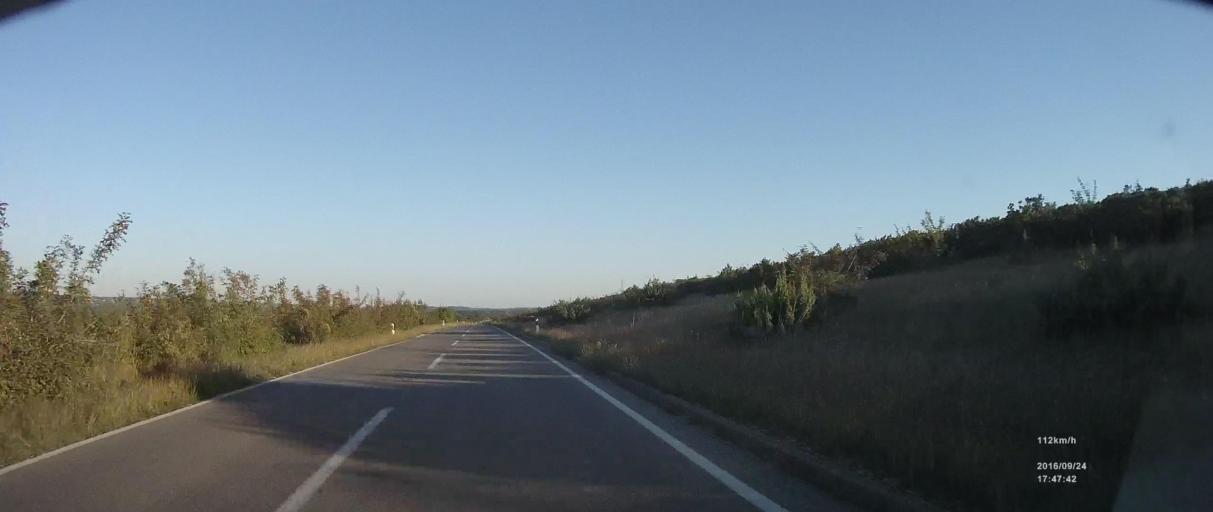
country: HR
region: Zadarska
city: Polaca
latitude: 44.0720
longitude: 15.5270
